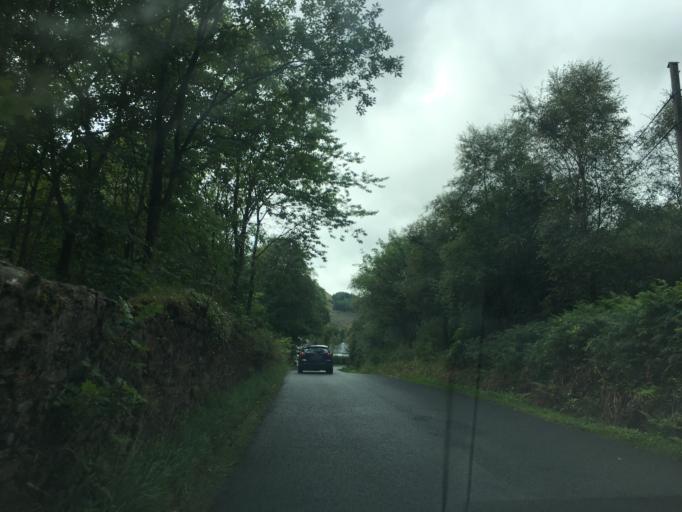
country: GB
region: Scotland
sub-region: Argyll and Bute
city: Dunoon
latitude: 55.9897
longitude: -5.0143
